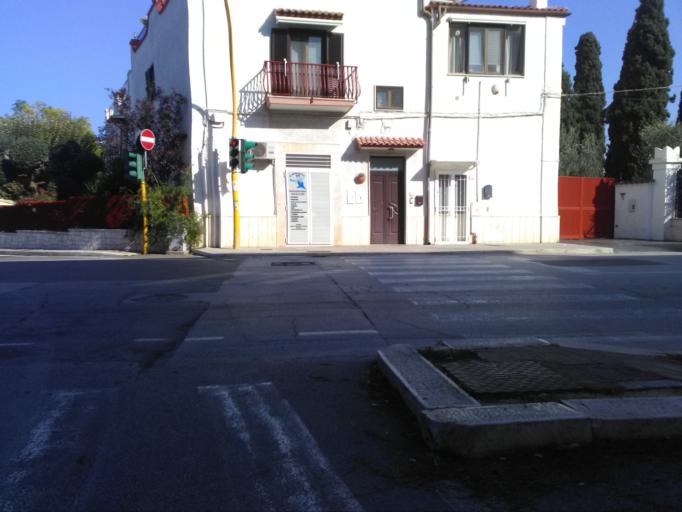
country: IT
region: Apulia
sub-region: Provincia di Bari
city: San Paolo
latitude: 41.1562
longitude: 16.7676
